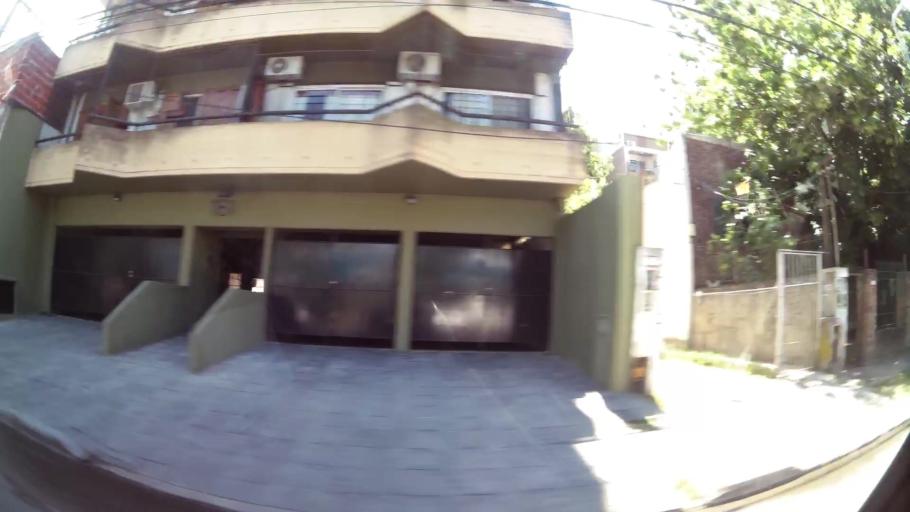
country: AR
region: Buenos Aires
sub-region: Partido de Tigre
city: Tigre
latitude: -34.4273
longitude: -58.5769
